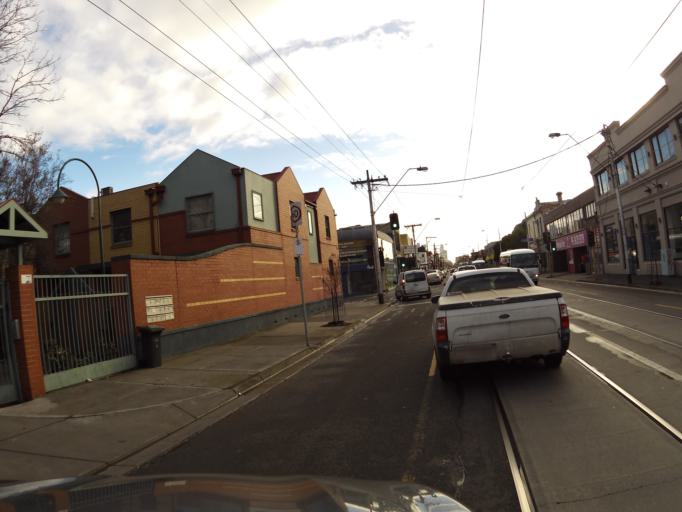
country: AU
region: Victoria
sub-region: Yarra
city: Richmond
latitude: -37.8110
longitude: 145.0056
